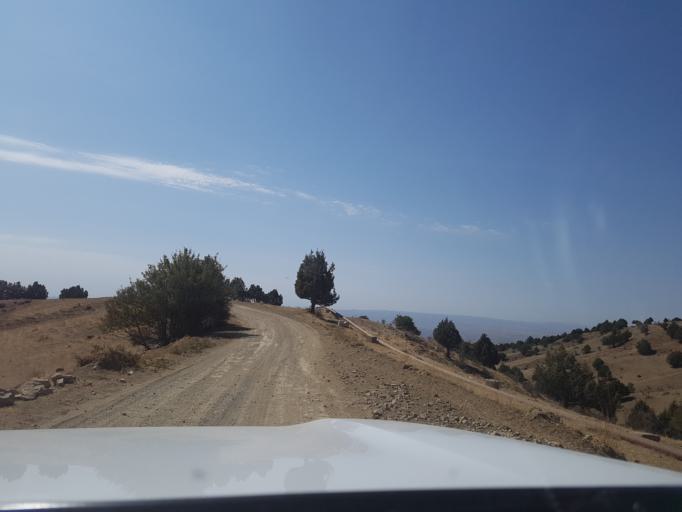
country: TM
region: Ahal
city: Baharly
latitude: 38.3195
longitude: 56.9548
